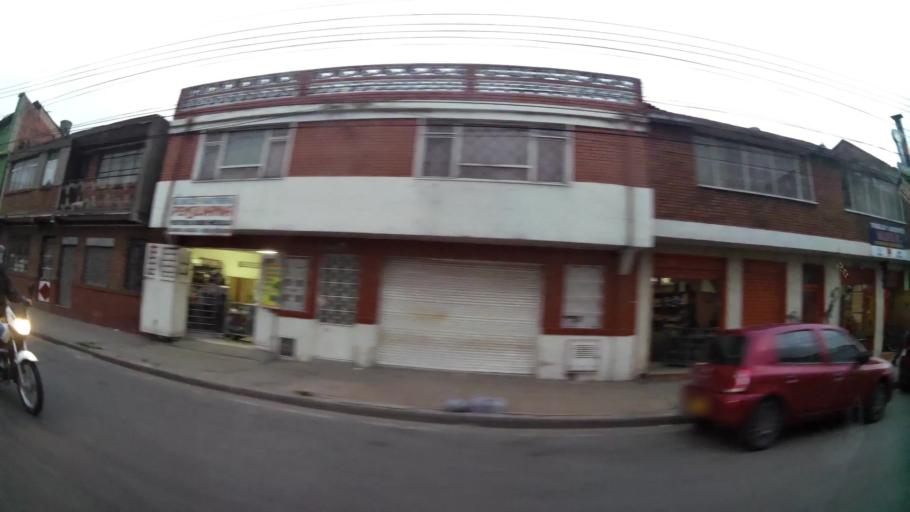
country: CO
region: Bogota D.C.
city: Bogota
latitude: 4.5847
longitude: -74.1236
